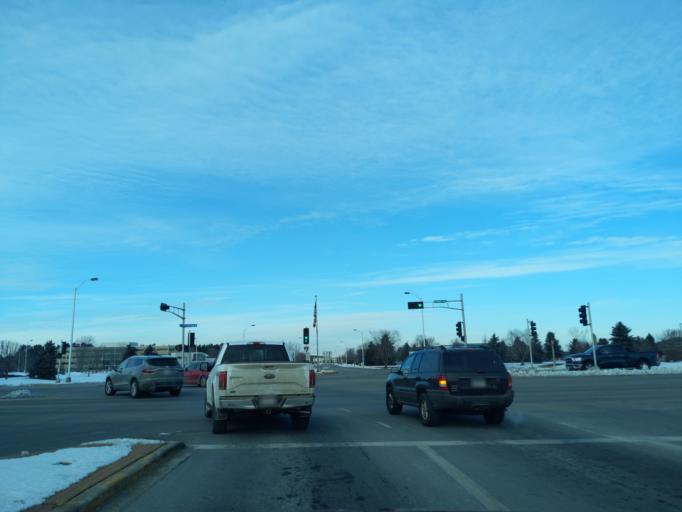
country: US
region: Wisconsin
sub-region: Portage County
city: Whiting
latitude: 44.4970
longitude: -89.5134
